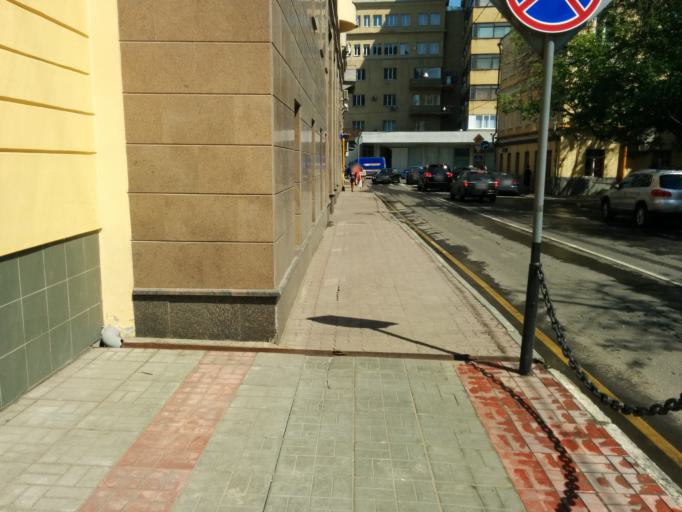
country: RU
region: Moscow
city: Zamoskvorech'ye
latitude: 55.7374
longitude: 37.6340
